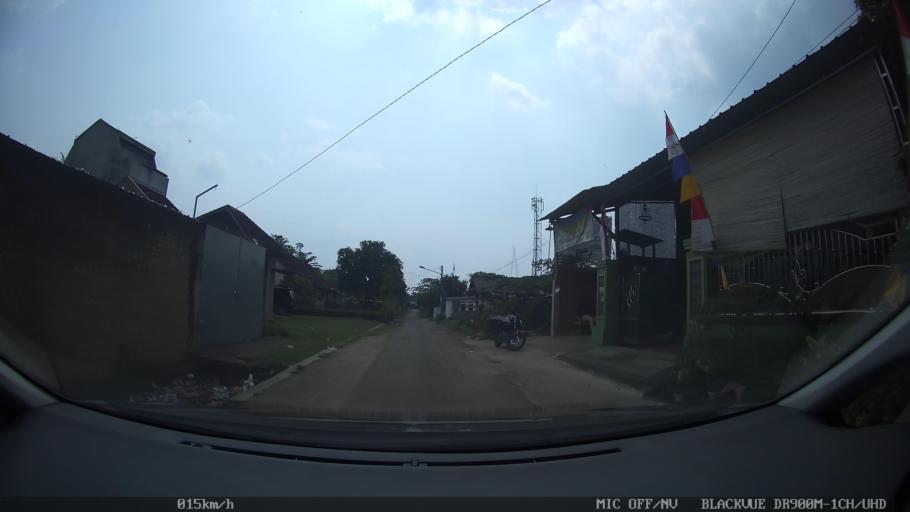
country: ID
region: Lampung
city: Gadingrejo
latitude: -5.3688
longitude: 105.0625
